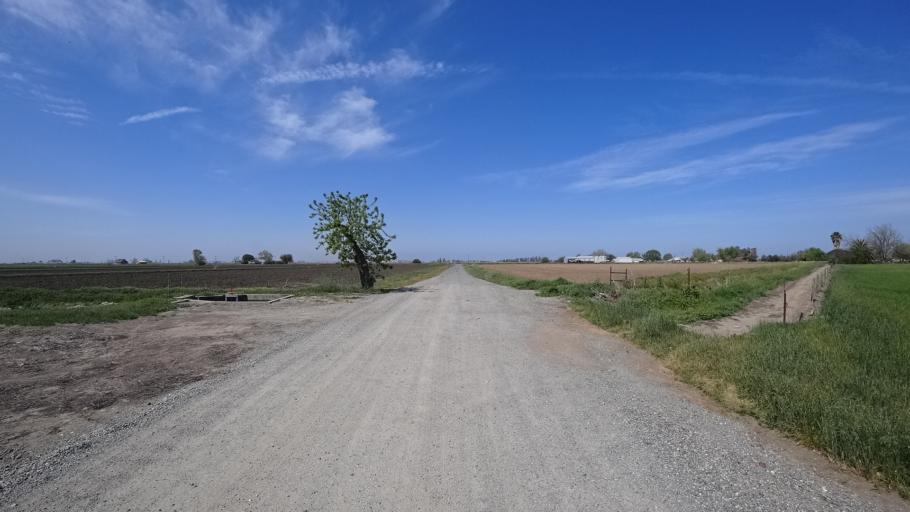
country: US
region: California
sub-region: Glenn County
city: Willows
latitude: 39.5798
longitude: -122.0422
